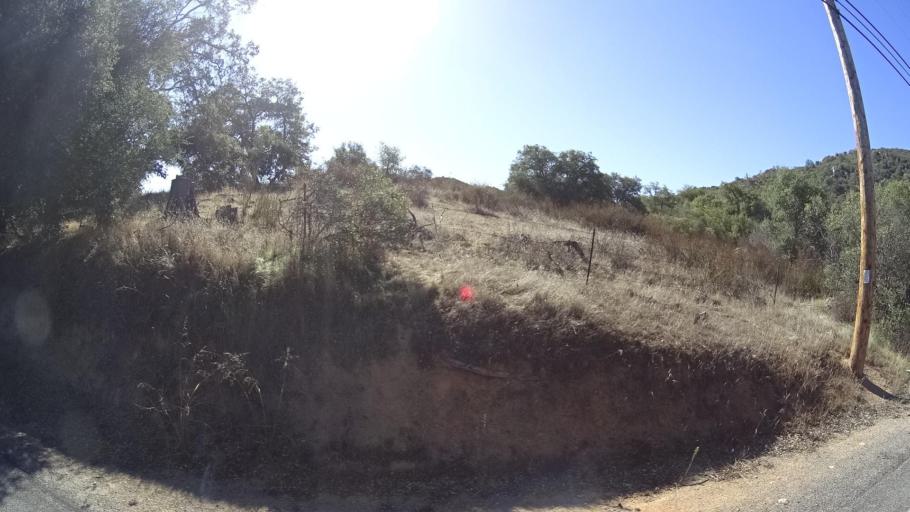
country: US
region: California
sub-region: San Diego County
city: Alpine
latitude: 32.7102
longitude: -116.7483
